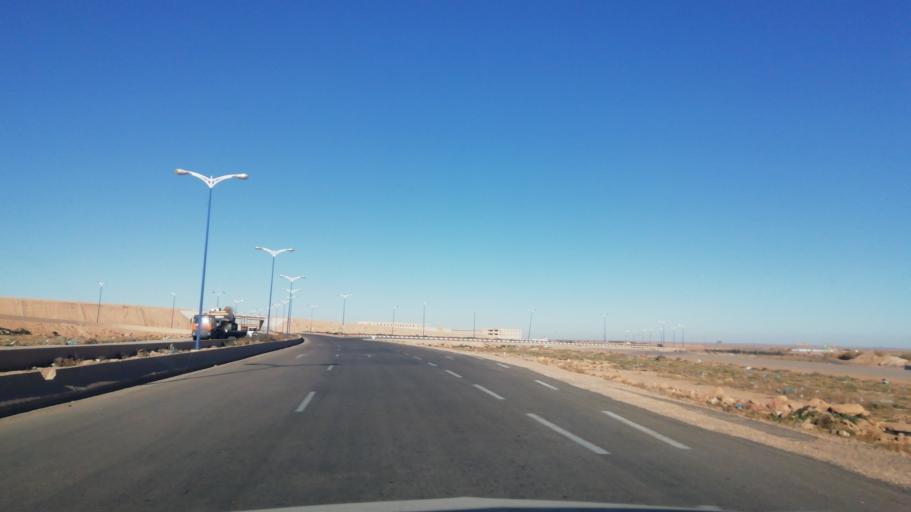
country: DZ
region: Wilaya de Naama
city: Naama
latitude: 33.5540
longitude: -0.2382
